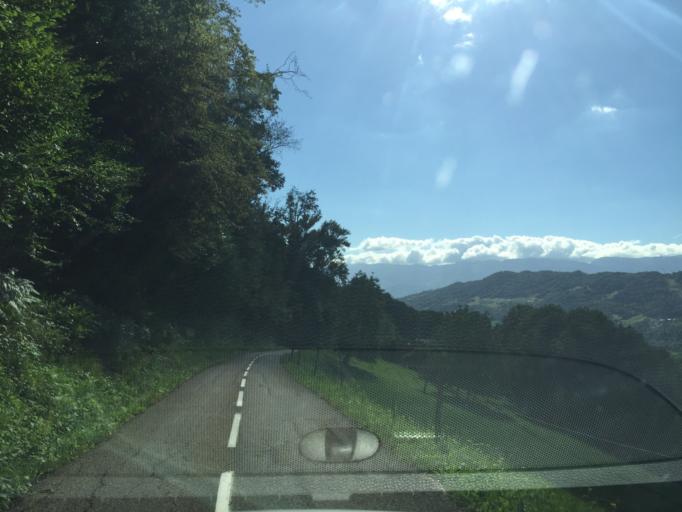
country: FR
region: Rhone-Alpes
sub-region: Departement de la Savoie
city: La Rochette
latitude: 45.4783
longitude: 6.1552
